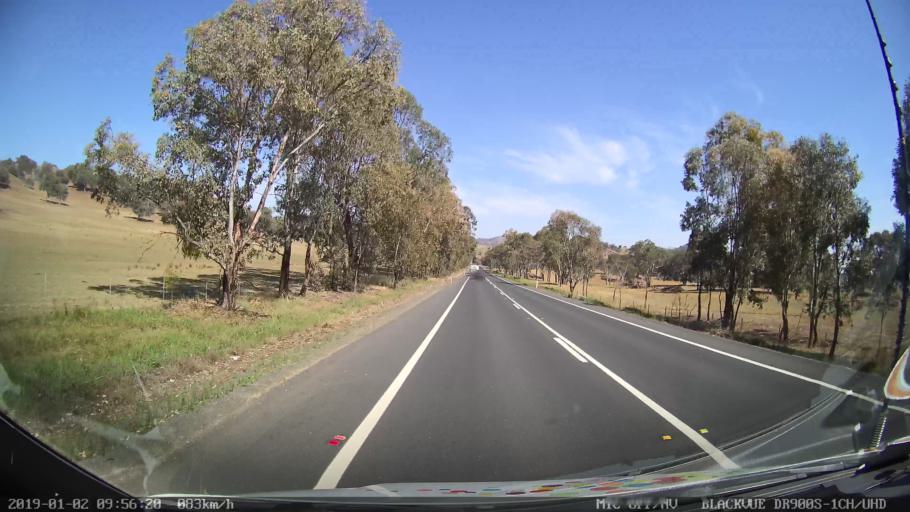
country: AU
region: New South Wales
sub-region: Tumut Shire
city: Tumut
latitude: -35.2160
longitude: 148.1778
